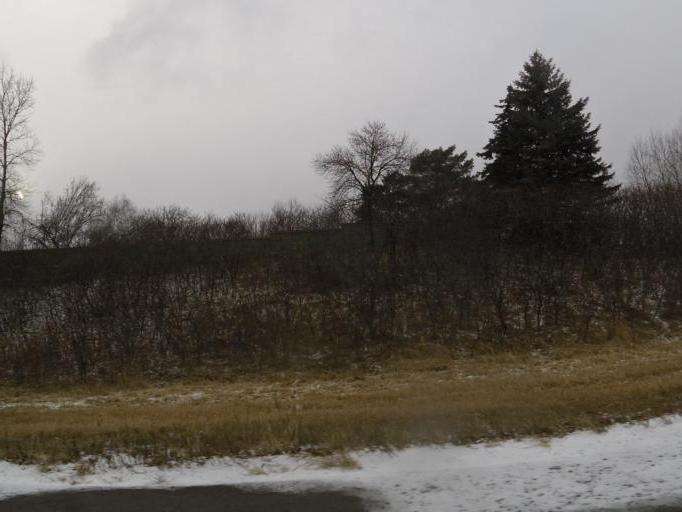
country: US
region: Minnesota
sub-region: Dakota County
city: Apple Valley
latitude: 44.7830
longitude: -93.2186
